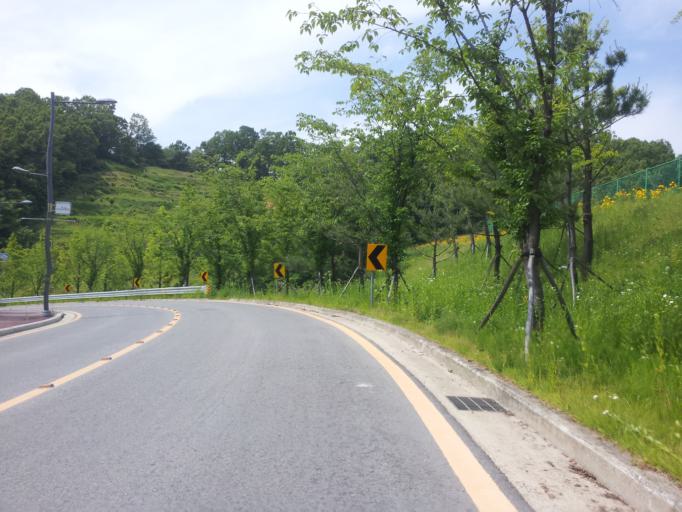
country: KR
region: Daejeon
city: Sintansin
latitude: 36.4574
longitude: 127.4751
